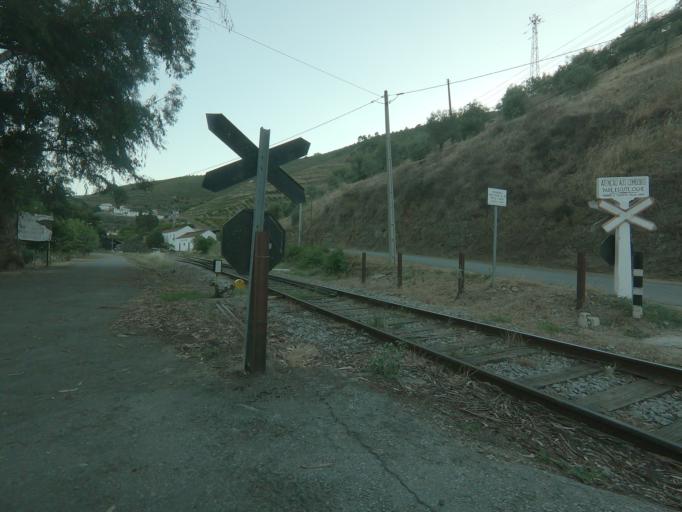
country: PT
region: Viseu
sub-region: Armamar
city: Armamar
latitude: 41.1539
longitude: -7.6860
